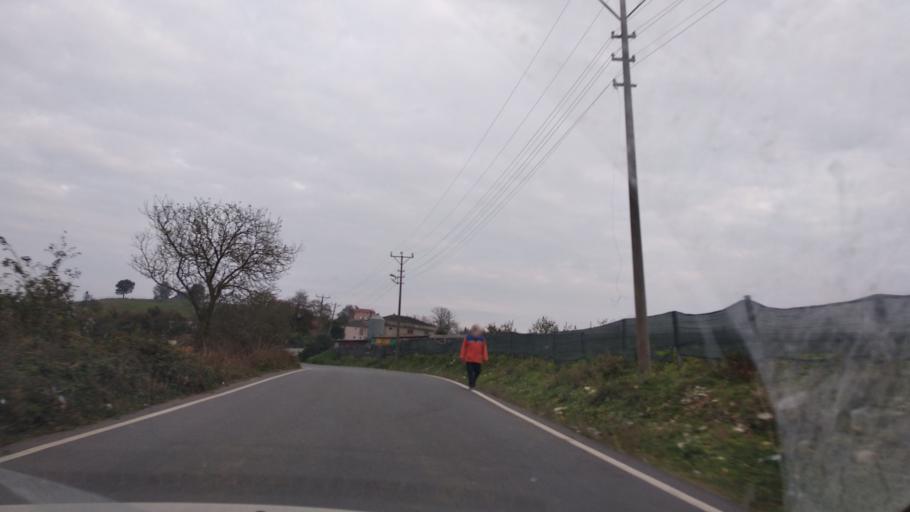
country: TR
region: Sakarya
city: Ortakoy
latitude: 41.0348
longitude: 30.6595
